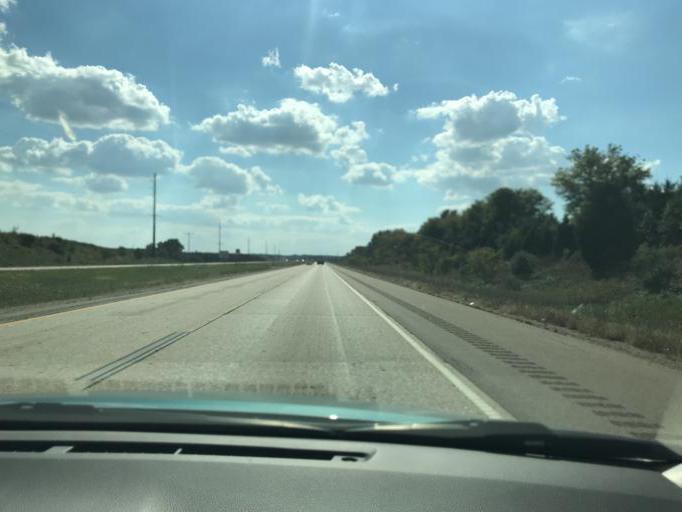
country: US
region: Wisconsin
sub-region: Walworth County
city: Delavan
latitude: 42.6208
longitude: -88.6284
